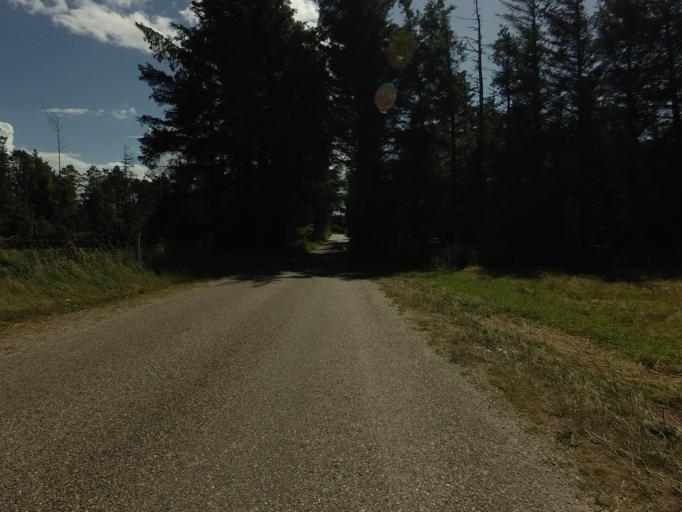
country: DK
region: North Denmark
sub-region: Jammerbugt Kommune
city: Pandrup
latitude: 57.3131
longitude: 9.6666
